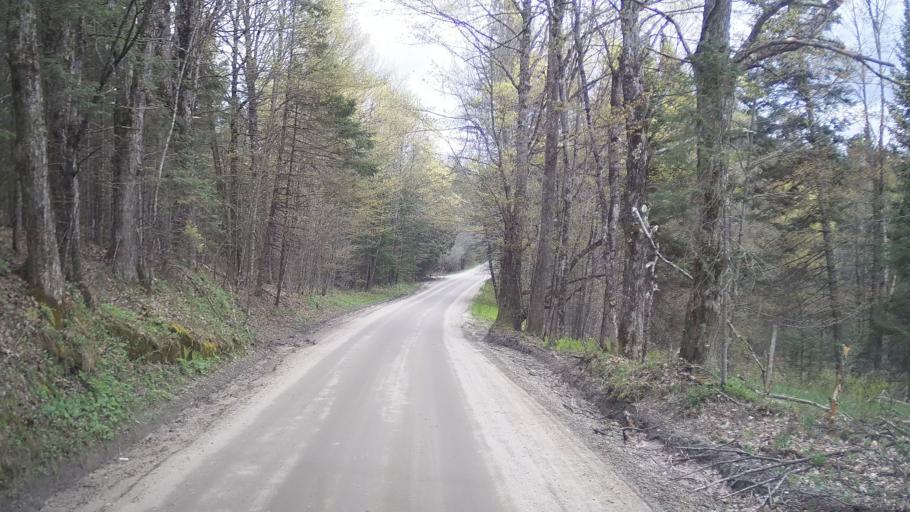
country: US
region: Vermont
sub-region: Caledonia County
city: Lyndonville
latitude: 44.6135
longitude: -71.9437
